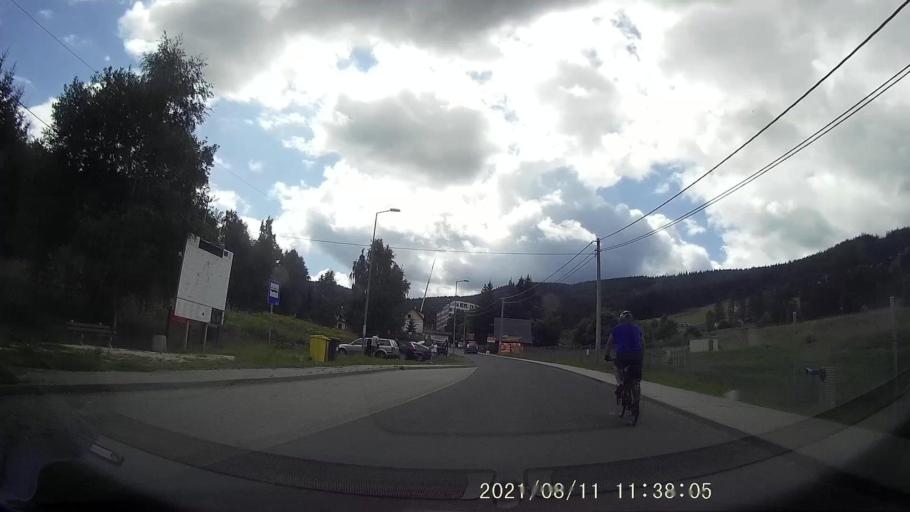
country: PL
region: Lower Silesian Voivodeship
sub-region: Powiat klodzki
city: Stronie Slaskie
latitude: 50.2606
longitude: 16.8231
